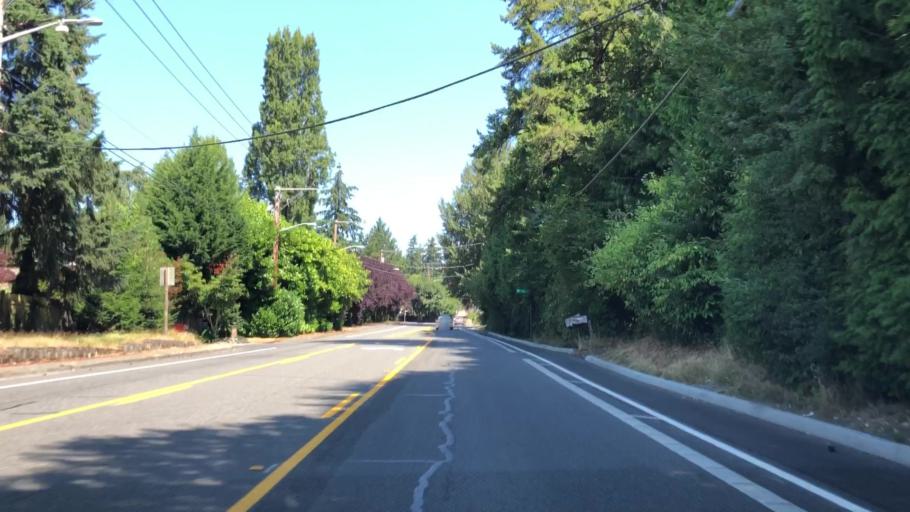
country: US
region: Washington
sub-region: King County
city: Inglewood-Finn Hill
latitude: 47.7102
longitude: -122.2381
